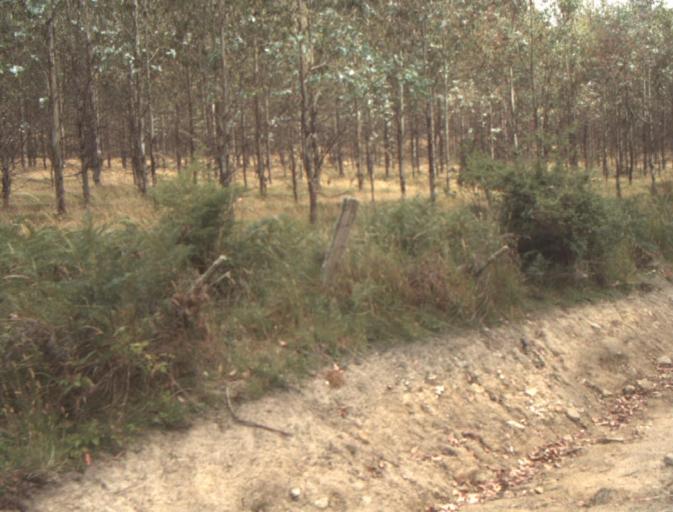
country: AU
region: Tasmania
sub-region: Northern Midlands
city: Evandale
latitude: -41.4562
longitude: 147.4453
